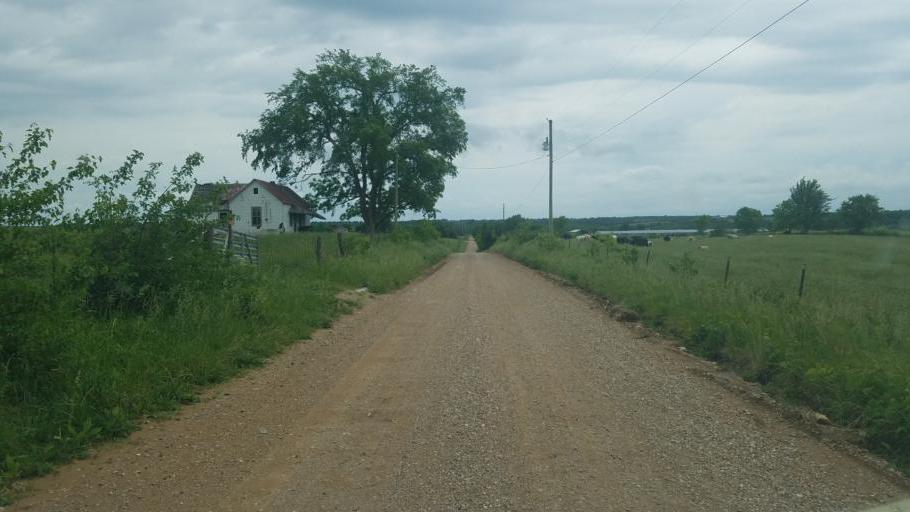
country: US
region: Missouri
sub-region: Moniteau County
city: California
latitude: 38.6198
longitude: -92.6193
